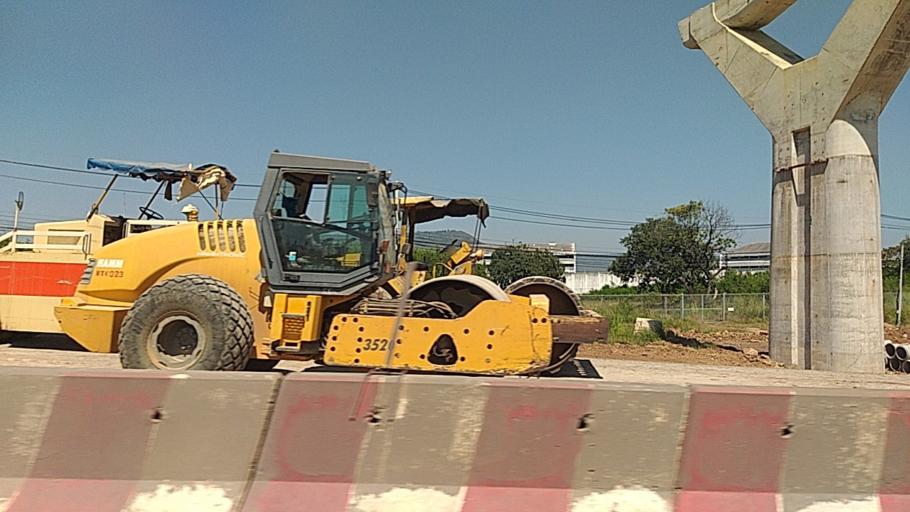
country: TH
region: Nakhon Ratchasima
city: Amphoe Sikhiu
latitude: 14.8510
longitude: 101.5739
